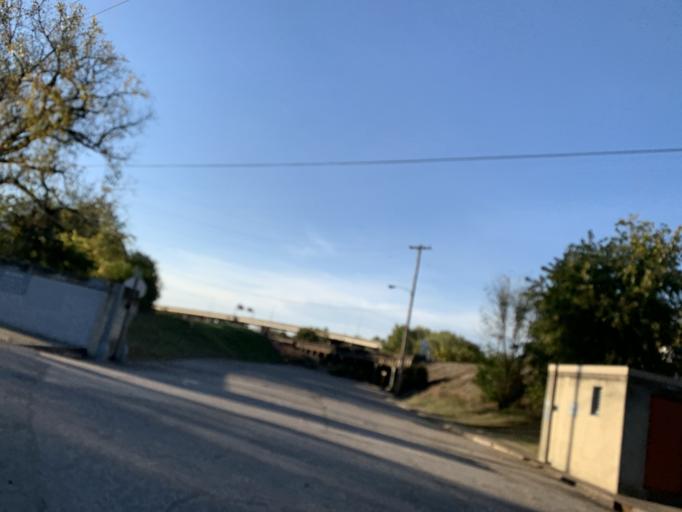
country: US
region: Indiana
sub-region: Floyd County
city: New Albany
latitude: 38.2752
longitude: -85.7970
